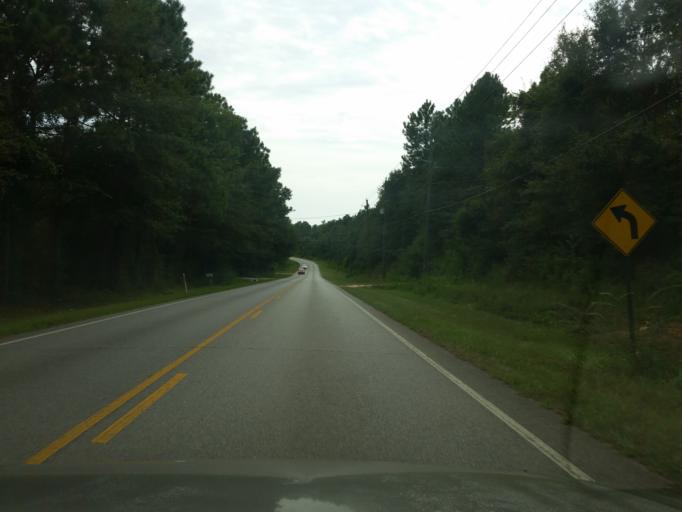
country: US
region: Florida
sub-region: Escambia County
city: Molino
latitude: 30.6668
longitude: -87.3208
